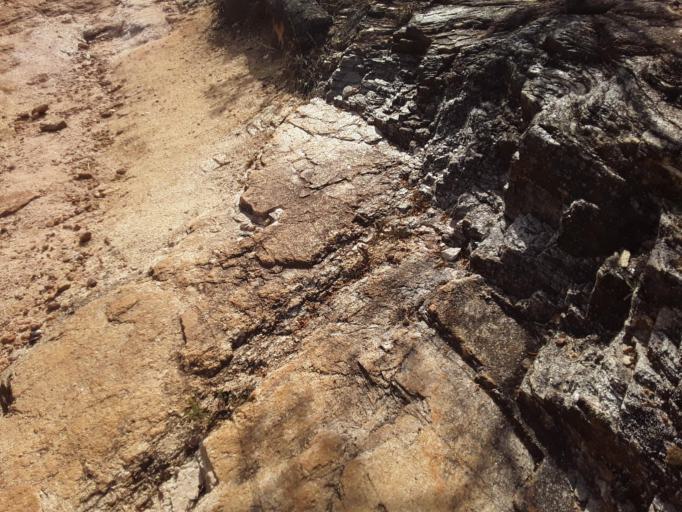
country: BR
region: Minas Gerais
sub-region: Lima Duarte
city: Lima Duarte
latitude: -21.7010
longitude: -43.8833
